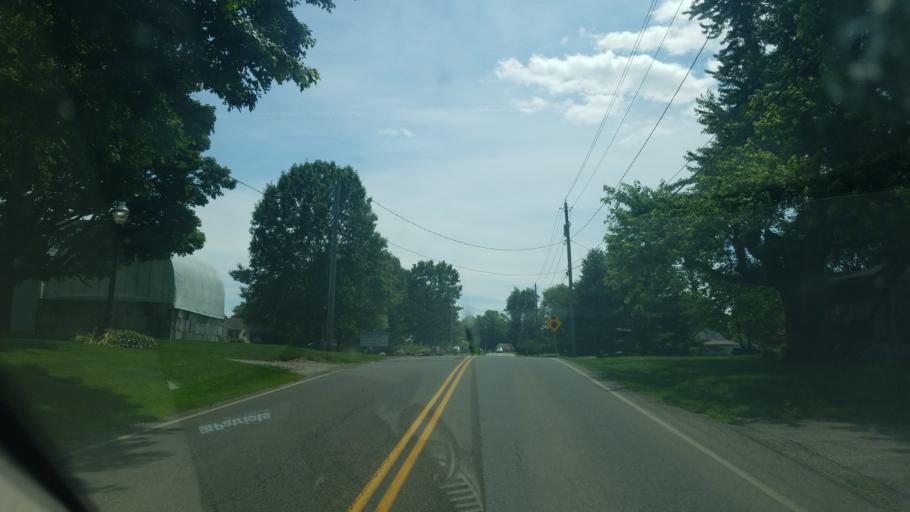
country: US
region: Ohio
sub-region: Stark County
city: Massillon
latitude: 40.8087
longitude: -81.5413
